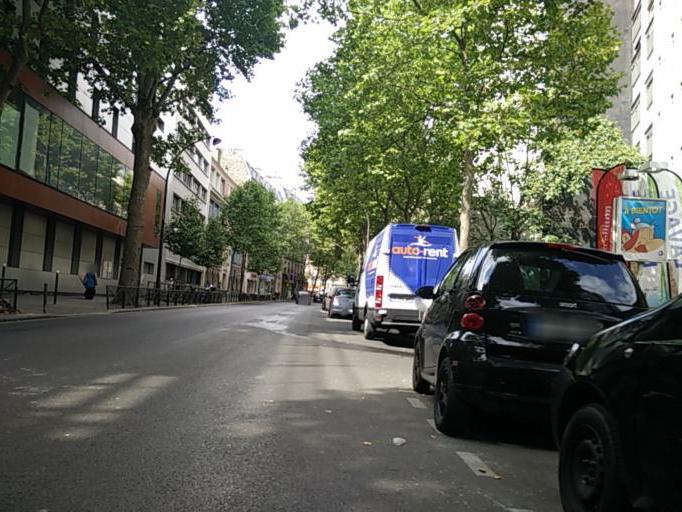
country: FR
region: Ile-de-France
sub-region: Departement de Seine-Saint-Denis
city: Le Pre-Saint-Gervais
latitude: 48.8837
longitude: 2.3898
